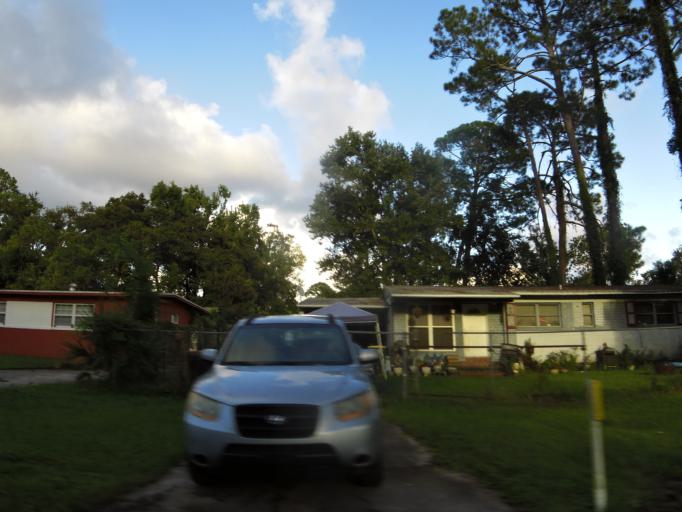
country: US
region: Florida
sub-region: Duval County
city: Jacksonville
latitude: 30.2754
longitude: -81.6188
